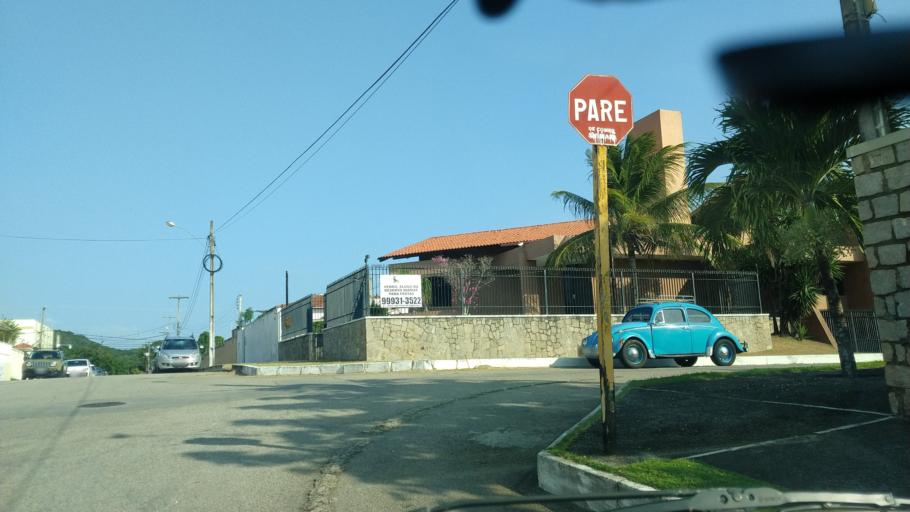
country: BR
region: Rio Grande do Norte
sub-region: Natal
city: Natal
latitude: -5.8446
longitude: -35.1981
